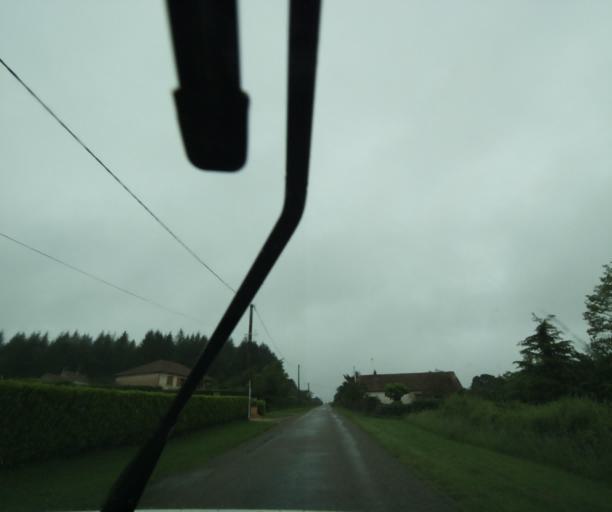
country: FR
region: Bourgogne
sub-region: Departement de Saone-et-Loire
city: Charolles
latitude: 46.4139
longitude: 4.2637
